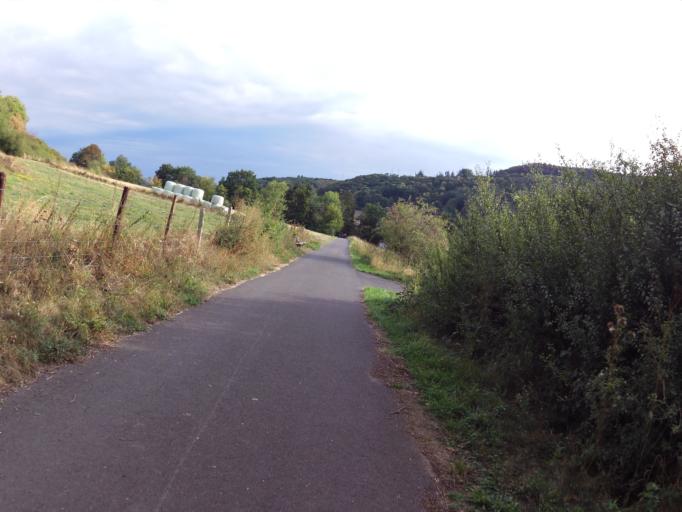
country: DE
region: North Rhine-Westphalia
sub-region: Regierungsbezirk Koln
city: Nideggen
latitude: 50.6780
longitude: 6.4697
